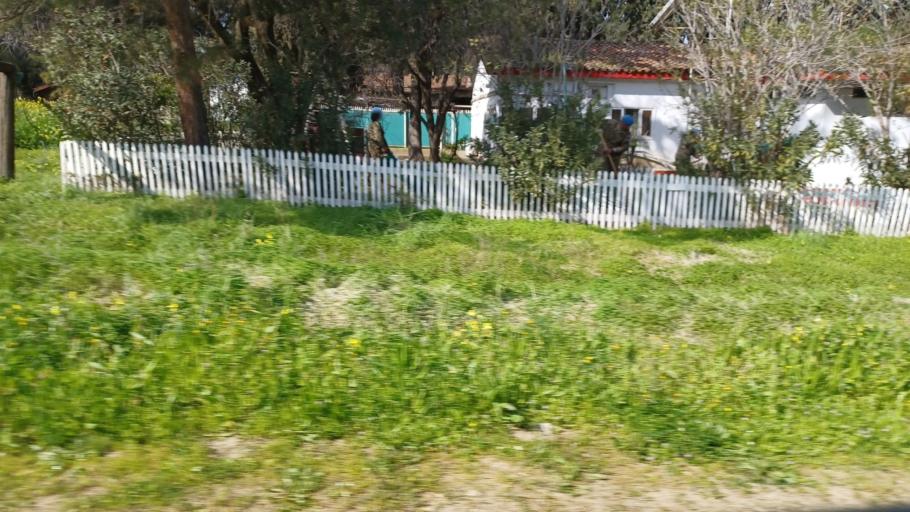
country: CY
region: Lefkosia
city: Lefka
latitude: 35.0911
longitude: 32.8871
